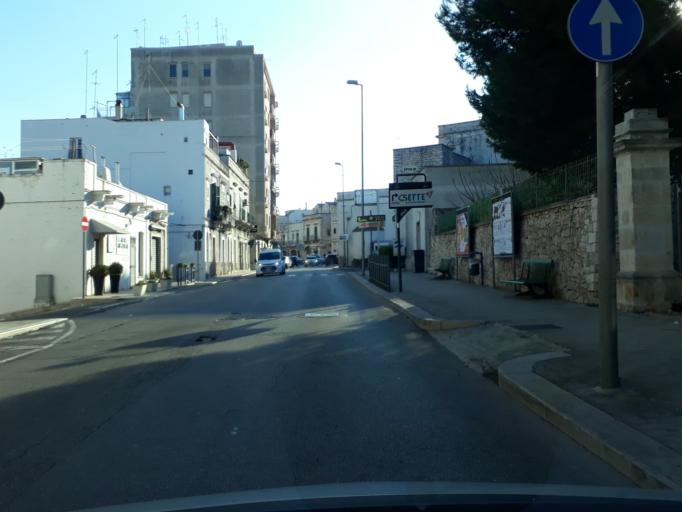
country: IT
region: Apulia
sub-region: Provincia di Bari
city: Locorotondo
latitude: 40.7575
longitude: 17.3270
